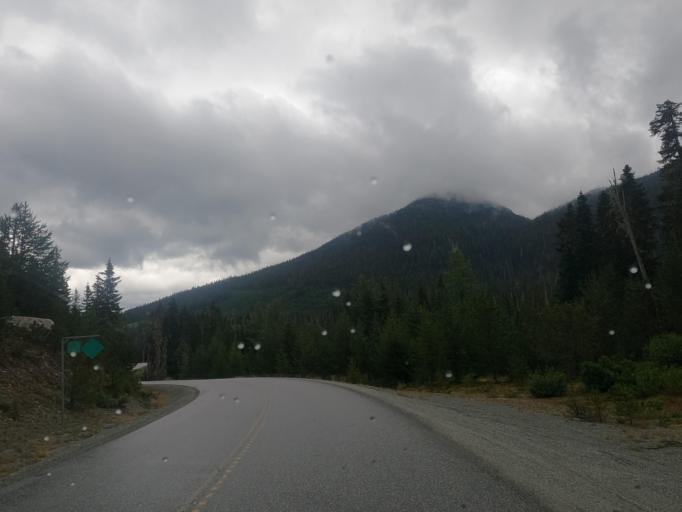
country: CA
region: British Columbia
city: Pemberton
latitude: 50.3804
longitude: -122.4786
